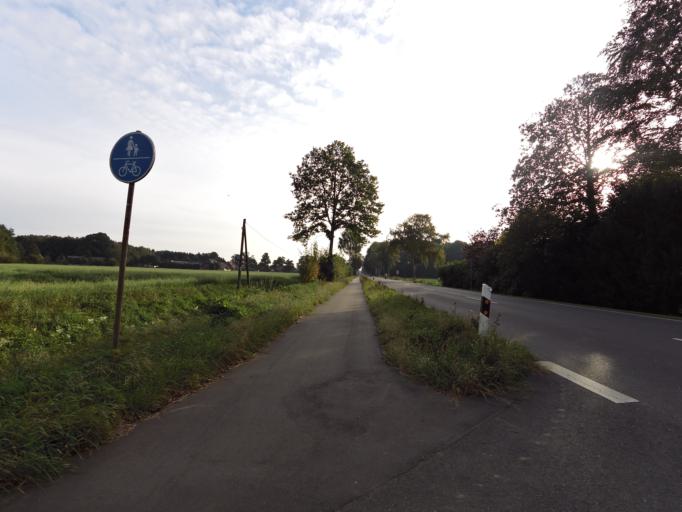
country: DE
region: North Rhine-Westphalia
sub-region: Regierungsbezirk Dusseldorf
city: Bocholt
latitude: 51.8049
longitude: 6.5618
